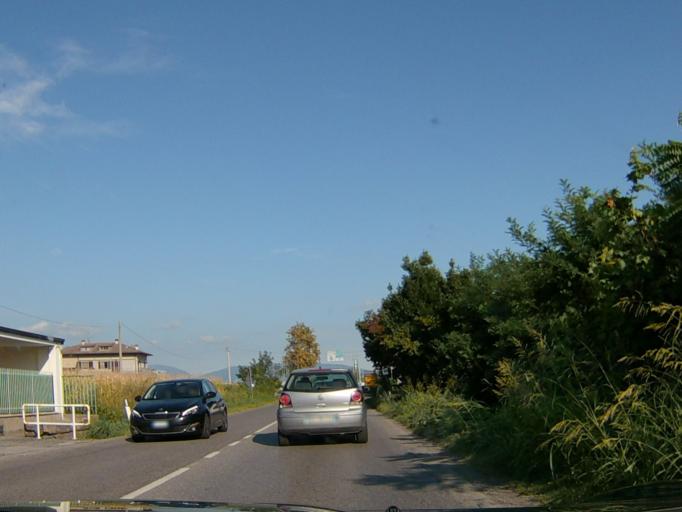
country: IT
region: Lombardy
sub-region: Provincia di Brescia
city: Lodetto
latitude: 45.5573
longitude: 10.0502
